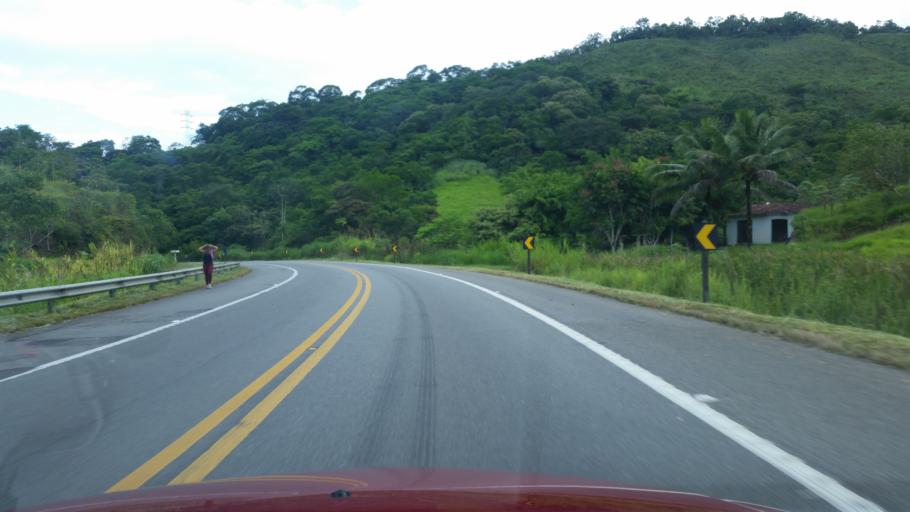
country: BR
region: Sao Paulo
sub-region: Miracatu
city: Miracatu
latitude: -24.2747
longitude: -47.2615
